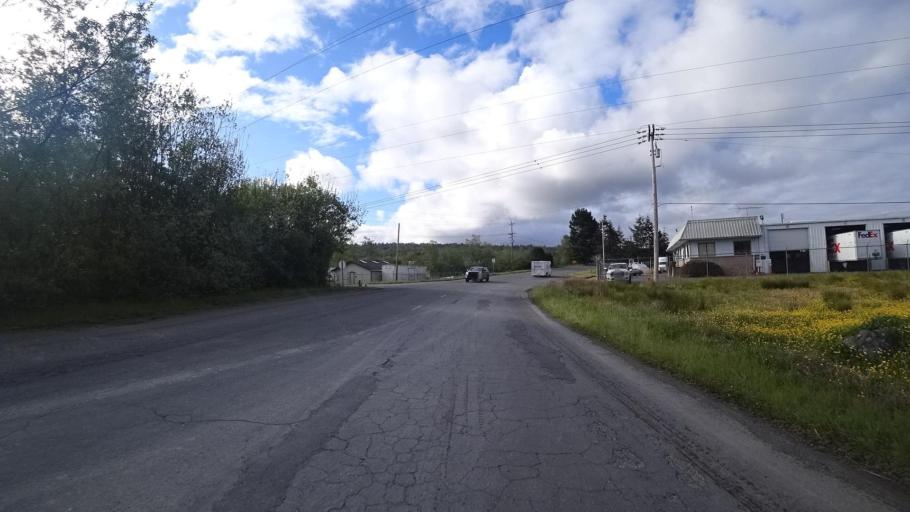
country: US
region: California
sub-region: Humboldt County
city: Arcata
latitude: 40.9052
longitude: -124.0720
